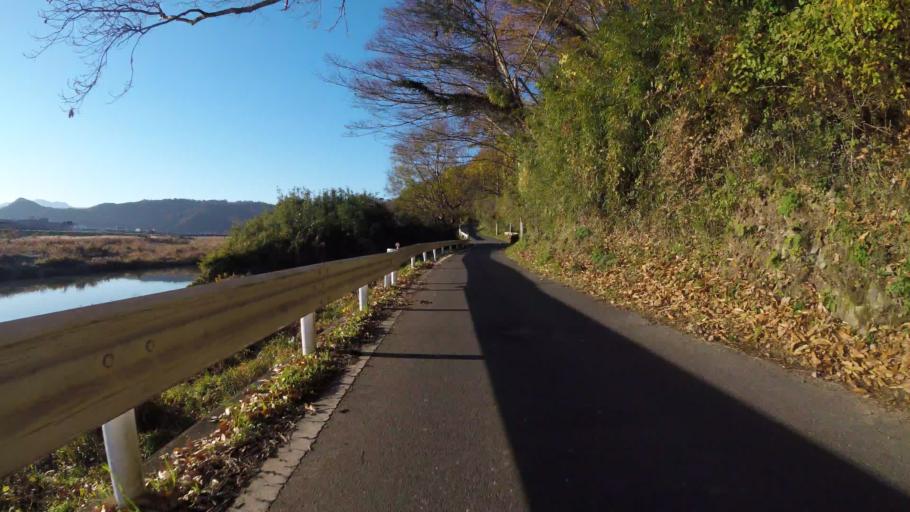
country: JP
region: Shizuoka
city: Mishima
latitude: 35.0038
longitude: 138.9340
